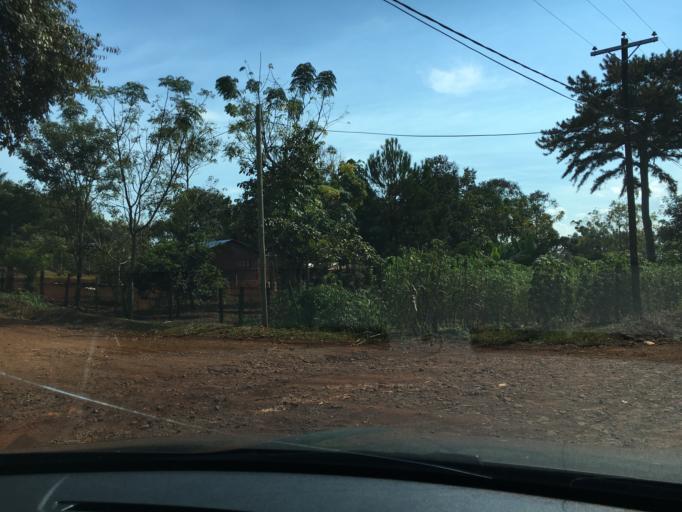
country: AR
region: Misiones
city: Puerto Rico
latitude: -26.8050
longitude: -54.9955
